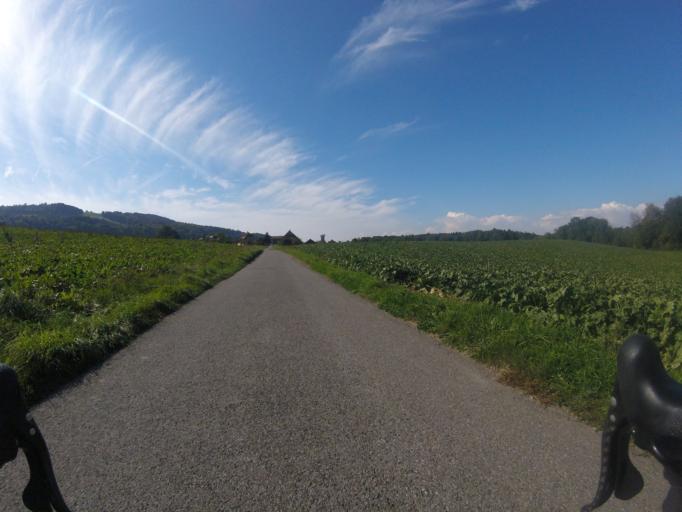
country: CH
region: Bern
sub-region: Bern-Mittelland District
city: Kehrsatz
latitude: 46.9215
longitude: 7.4723
